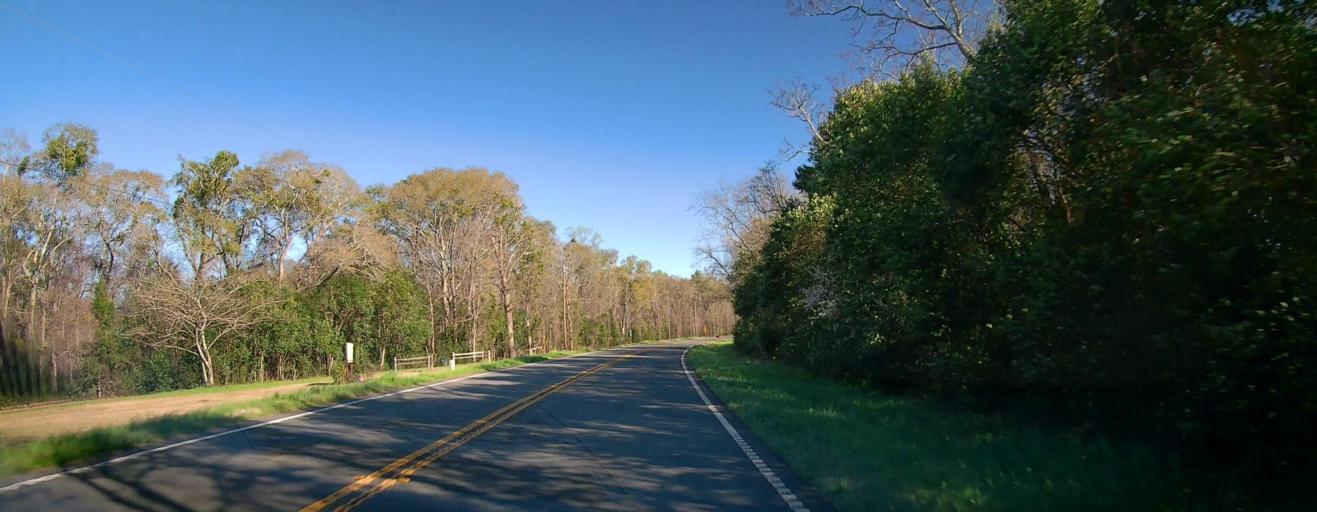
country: US
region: Georgia
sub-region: Macon County
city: Marshallville
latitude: 32.4547
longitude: -83.9147
